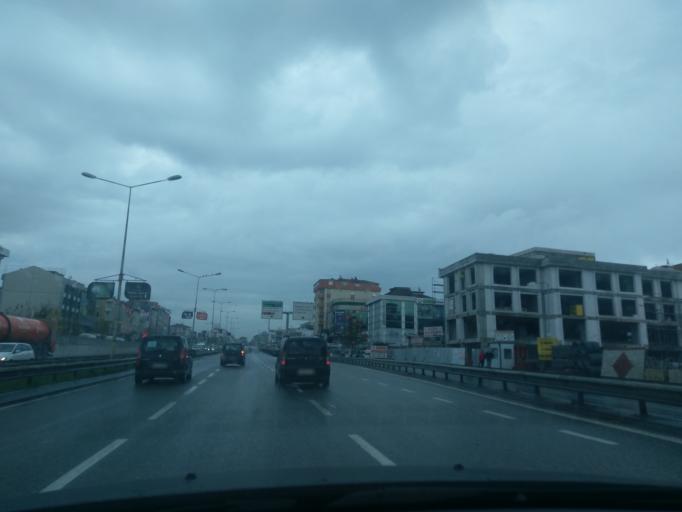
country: TR
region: Istanbul
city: Samandira
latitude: 41.0146
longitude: 29.1846
